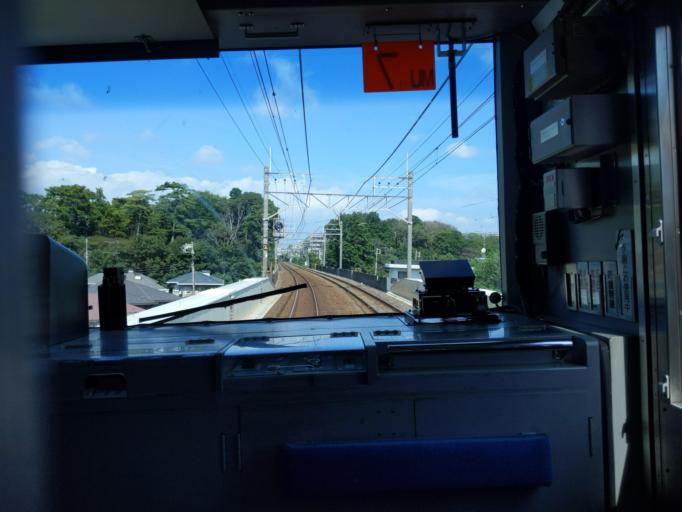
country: JP
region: Chiba
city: Funabashi
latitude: 35.7225
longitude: 139.9681
